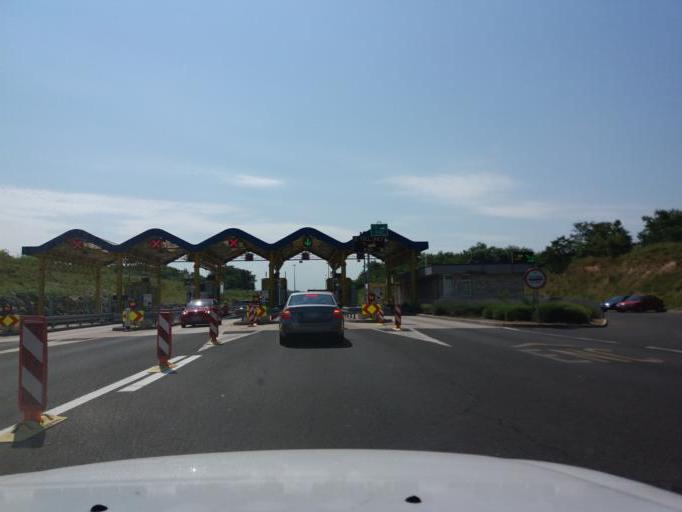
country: HR
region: Zadarska
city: Policnik
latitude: 44.1905
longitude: 15.4278
